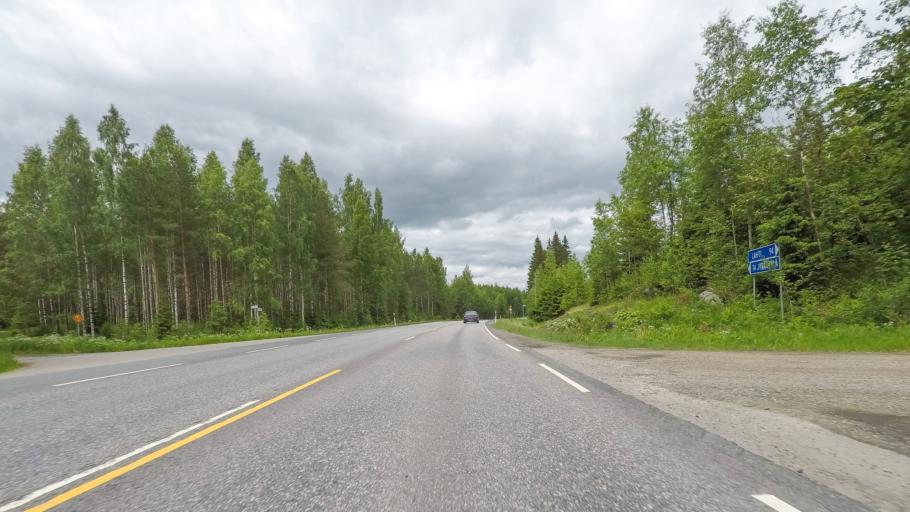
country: FI
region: Central Finland
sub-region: Joutsa
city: Joutsa
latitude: 61.6974
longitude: 26.0572
